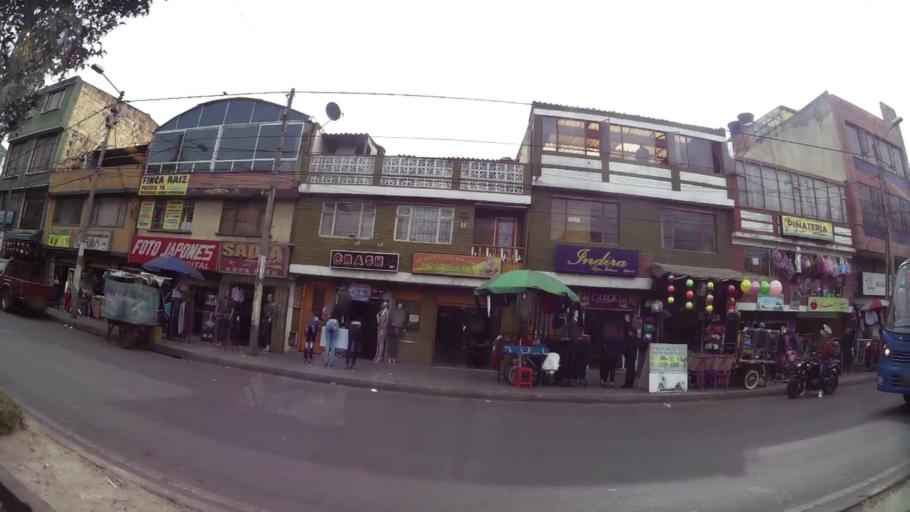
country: CO
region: Cundinamarca
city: Soacha
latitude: 4.6361
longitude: -74.1645
